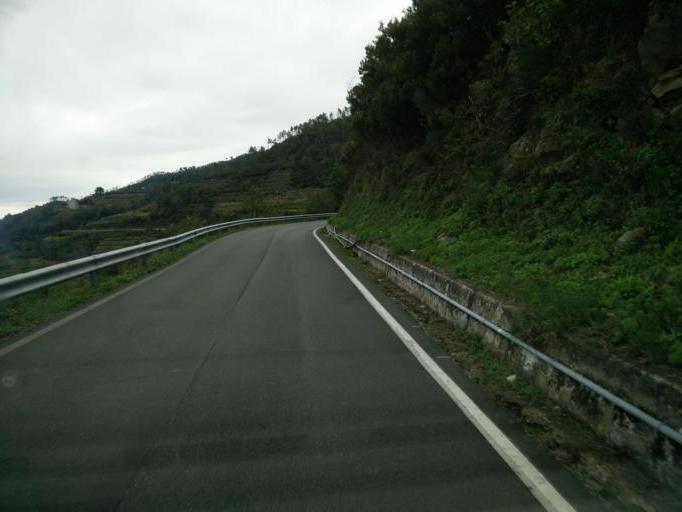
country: IT
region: Liguria
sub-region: Provincia di La Spezia
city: Riomaggiore
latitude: 44.1174
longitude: 9.7263
